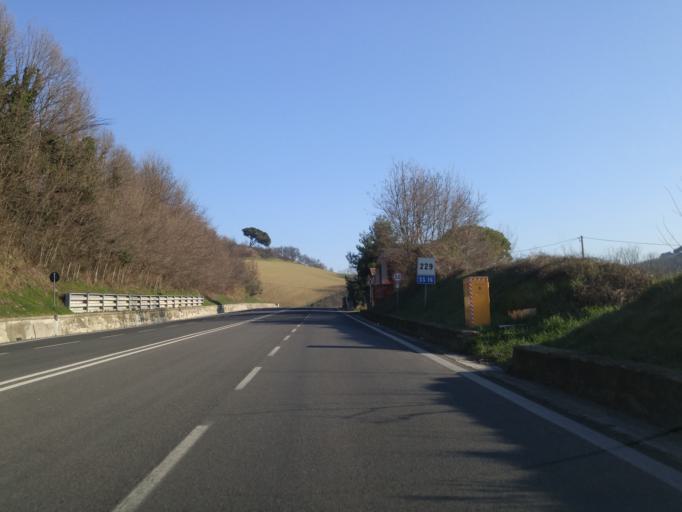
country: IT
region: The Marches
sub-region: Provincia di Pesaro e Urbino
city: Gradara
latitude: 43.9468
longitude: 12.8159
